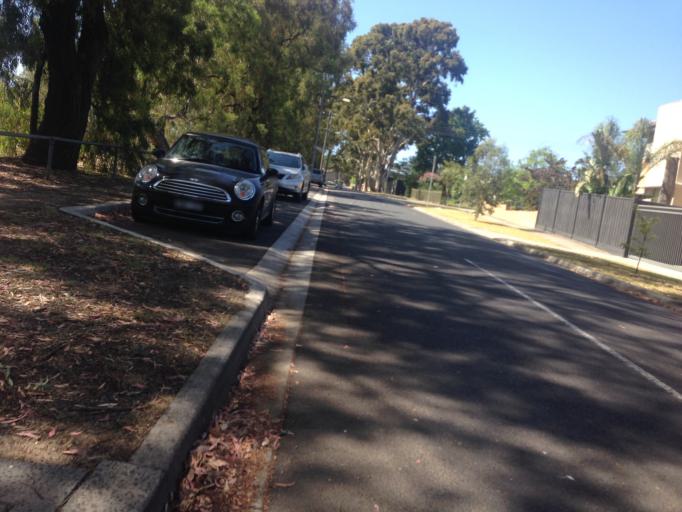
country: AU
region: Victoria
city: Ivanhoe East
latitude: -37.7739
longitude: 145.0530
